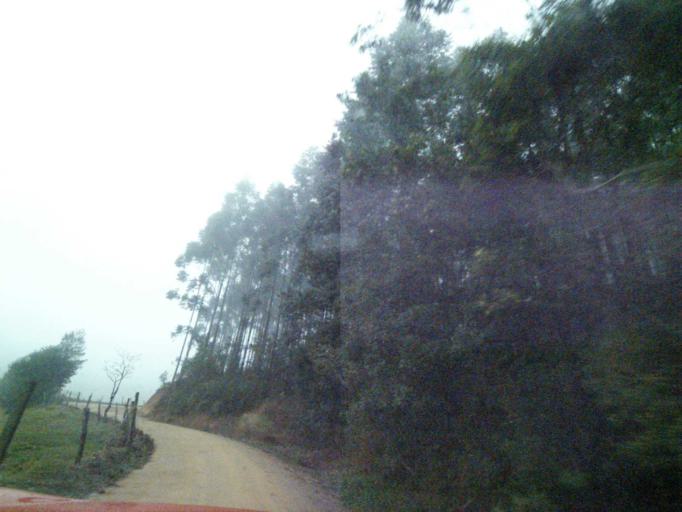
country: BR
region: Santa Catarina
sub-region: Anitapolis
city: Anitapolis
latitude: -27.9134
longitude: -49.1155
